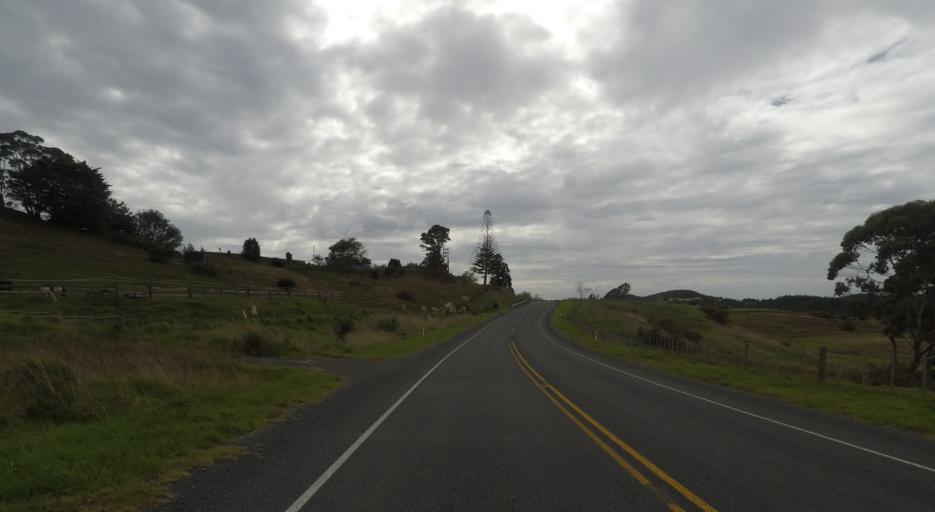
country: NZ
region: Auckland
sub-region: Auckland
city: Rothesay Bay
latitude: -36.6557
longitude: 174.6870
